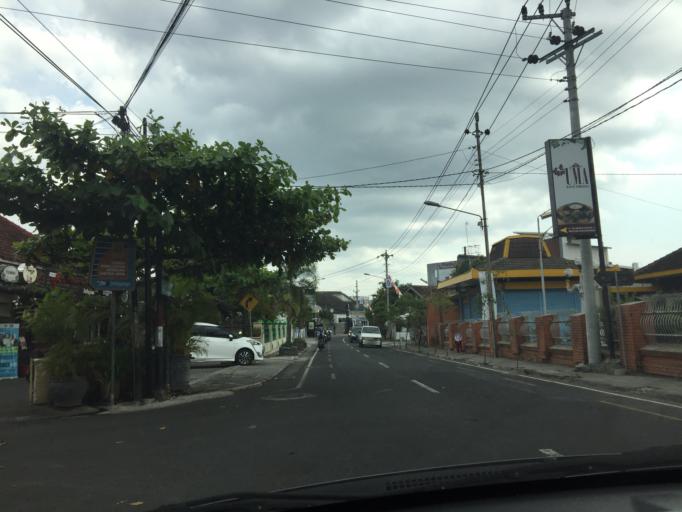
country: ID
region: Daerah Istimewa Yogyakarta
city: Yogyakarta
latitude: -7.7788
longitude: 110.3633
